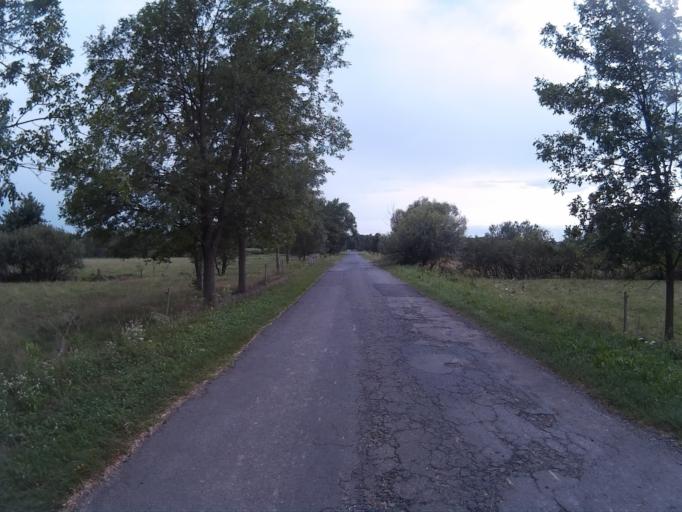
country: SI
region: Kobilje
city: Kobilje
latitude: 46.7312
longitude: 16.4204
